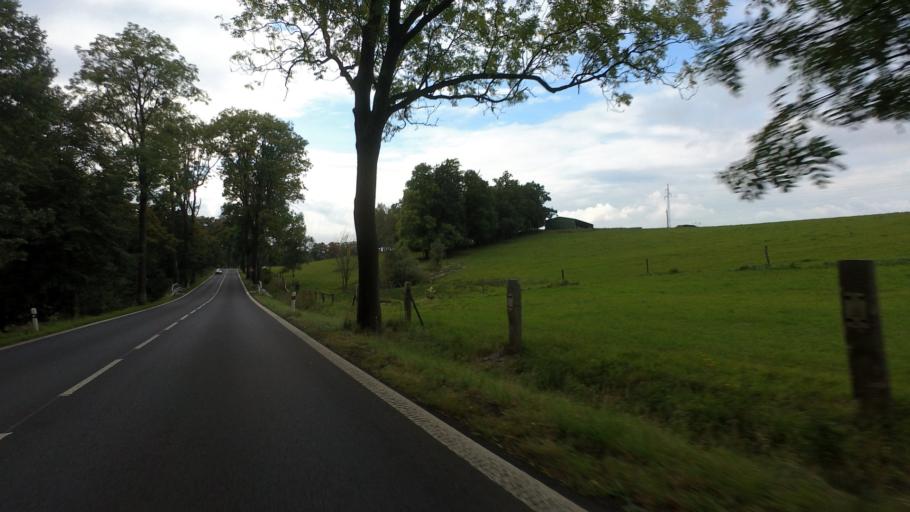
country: CZ
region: Ustecky
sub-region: Okres Decin
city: Sluknov
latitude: 50.9900
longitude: 14.4877
